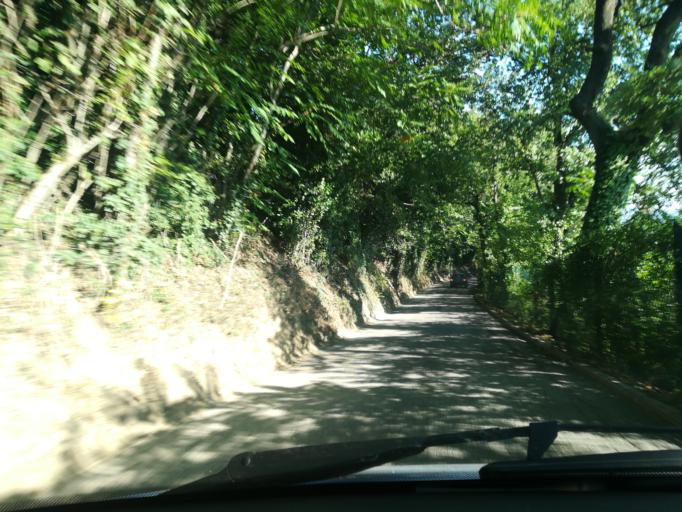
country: IT
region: The Marches
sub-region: Provincia di Macerata
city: Piediripa
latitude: 43.2957
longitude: 13.4836
